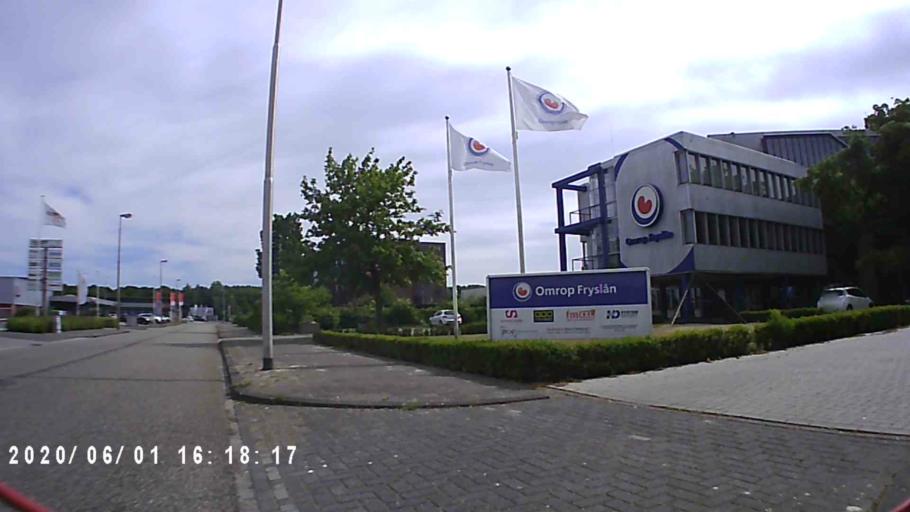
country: NL
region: Friesland
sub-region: Gemeente Leeuwarden
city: Camminghaburen
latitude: 53.1943
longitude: 5.8453
